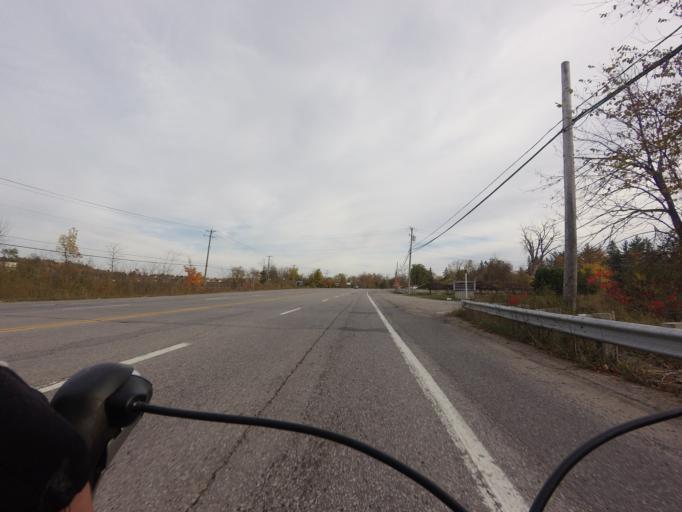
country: CA
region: Quebec
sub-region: Outaouais
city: Gatineau
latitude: 45.4805
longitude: -75.7464
